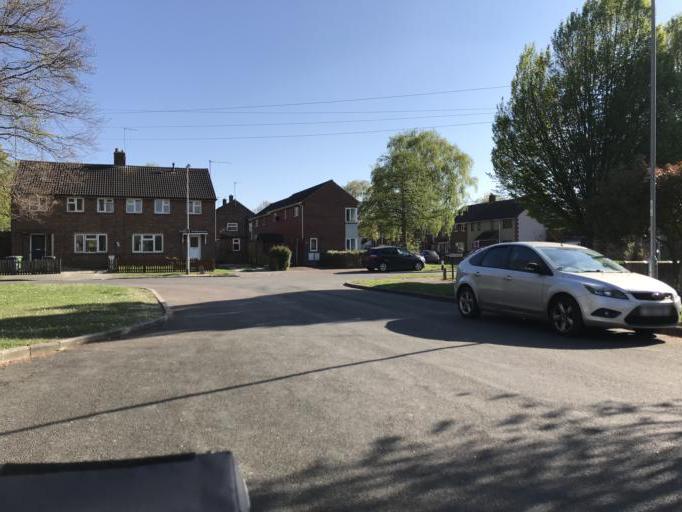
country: GB
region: England
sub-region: Cambridgeshire
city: Cambridge
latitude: 52.2095
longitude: 0.1609
